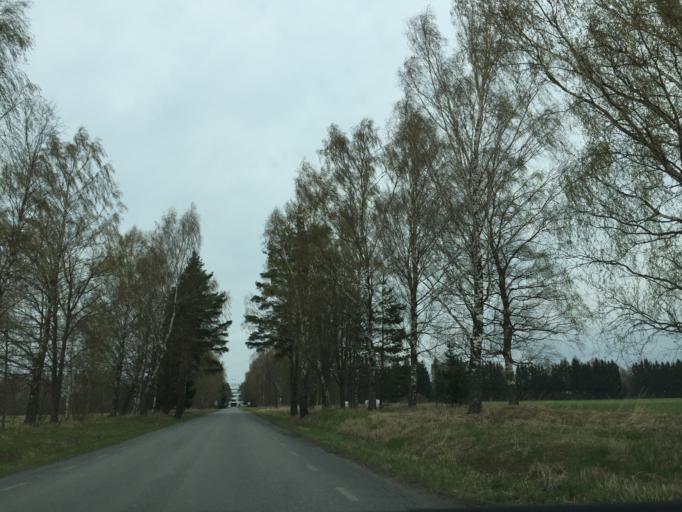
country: EE
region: Tartu
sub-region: Elva linn
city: Elva
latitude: 58.2618
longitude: 26.4707
